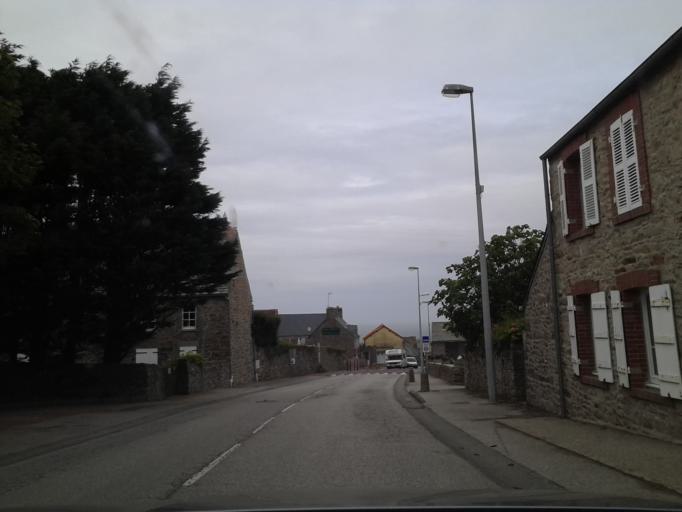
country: FR
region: Lower Normandy
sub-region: Departement de la Manche
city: Beaumont-Hague
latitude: 49.7107
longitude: -1.9321
